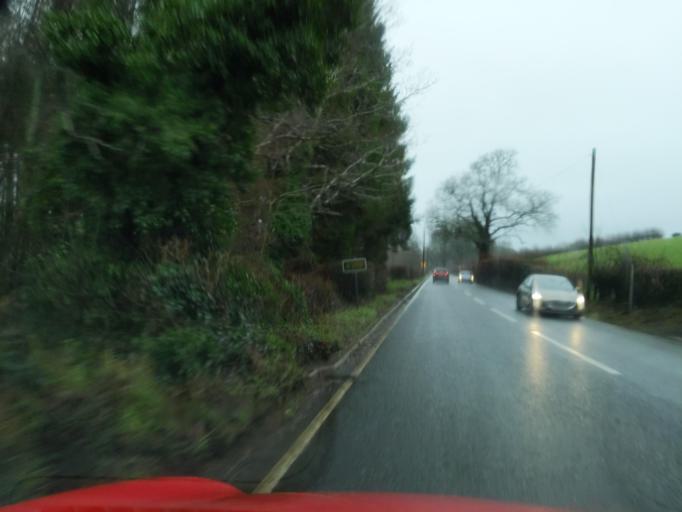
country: GB
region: England
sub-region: Cornwall
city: South Hill
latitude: 50.5801
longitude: -4.3329
